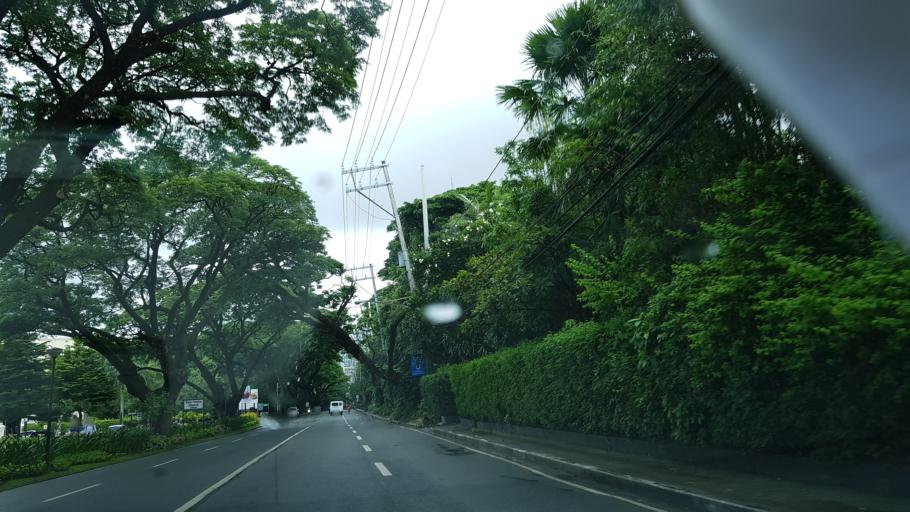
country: PH
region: Metro Manila
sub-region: Makati City
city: Makati City
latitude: 14.5473
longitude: 121.0353
